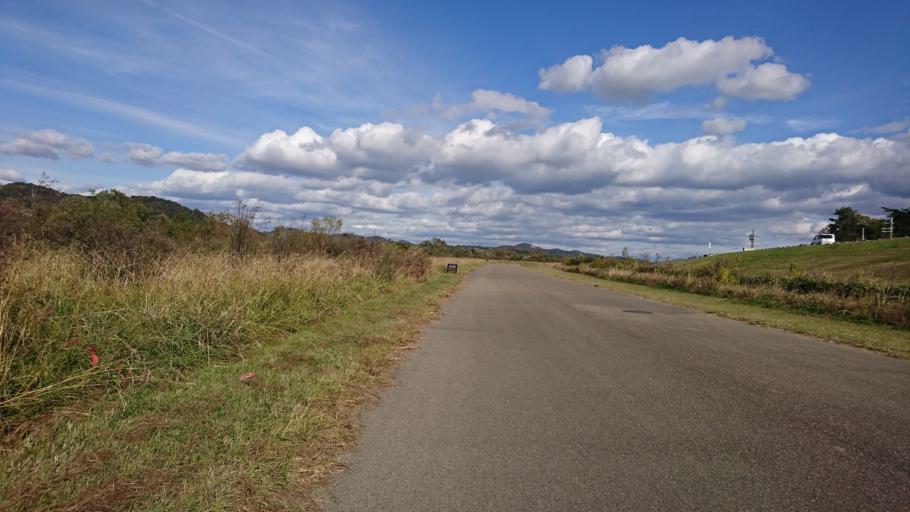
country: JP
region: Hyogo
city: Kakogawacho-honmachi
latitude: 34.7930
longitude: 134.8720
